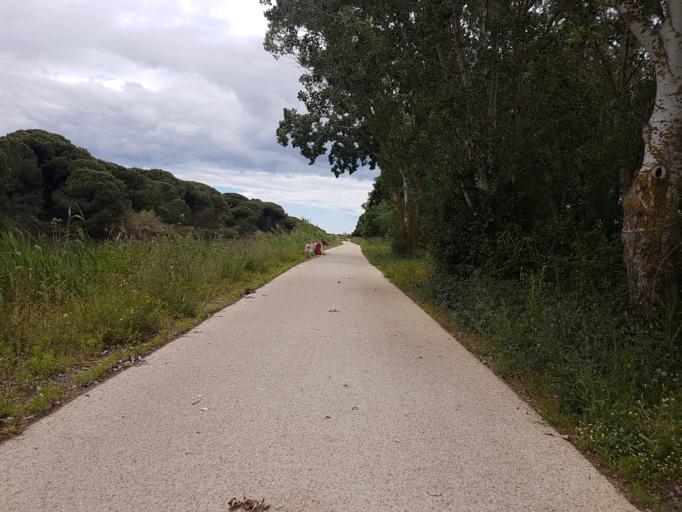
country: FR
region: Languedoc-Roussillon
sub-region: Departement du Gard
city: Aigues-Mortes
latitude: 43.5862
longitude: 4.2140
